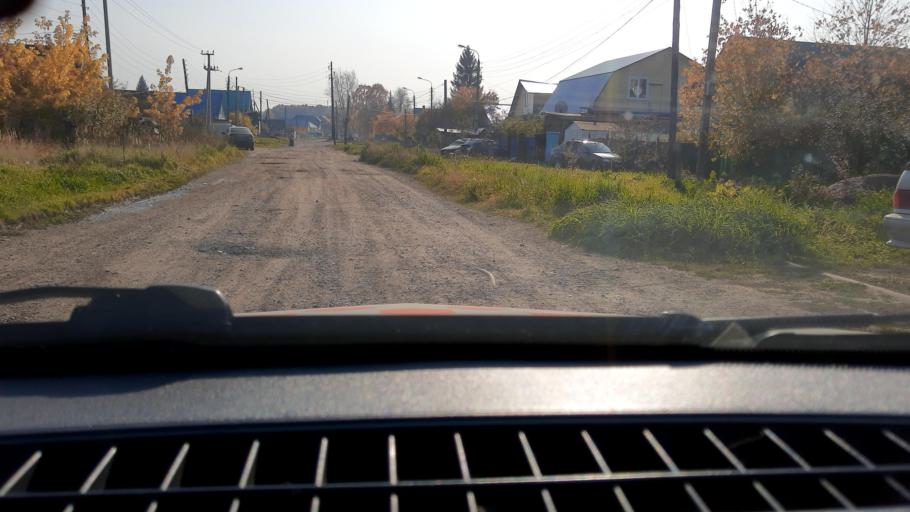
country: RU
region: Bashkortostan
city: Ufa
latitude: 54.8445
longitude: 56.1556
